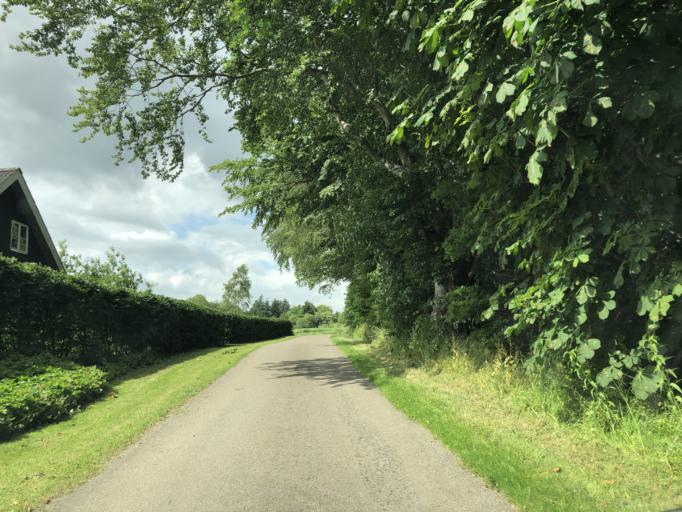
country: DK
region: Central Jutland
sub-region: Odder Kommune
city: Odder
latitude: 55.9686
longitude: 10.0937
